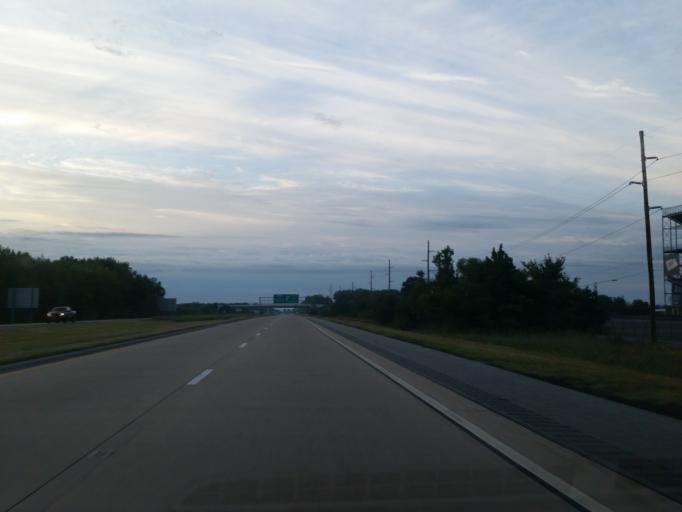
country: US
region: Delaware
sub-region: Kent County
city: Dover
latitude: 39.1953
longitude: -75.5304
